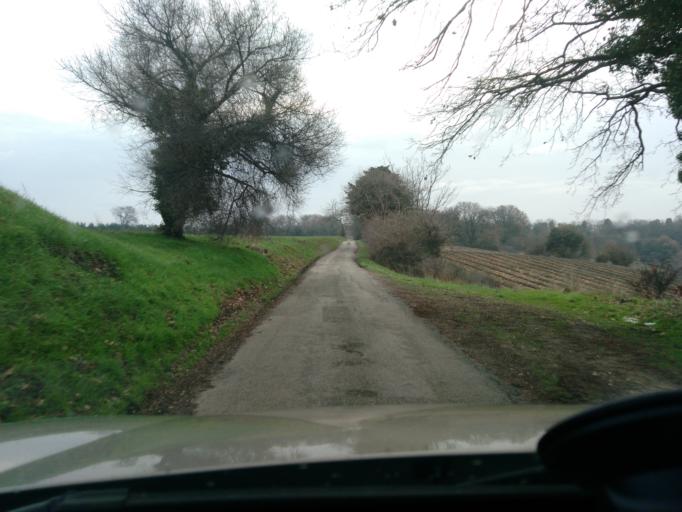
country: FR
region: Rhone-Alpes
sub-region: Departement de la Drome
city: Montelimar
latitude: 44.5746
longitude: 4.7713
